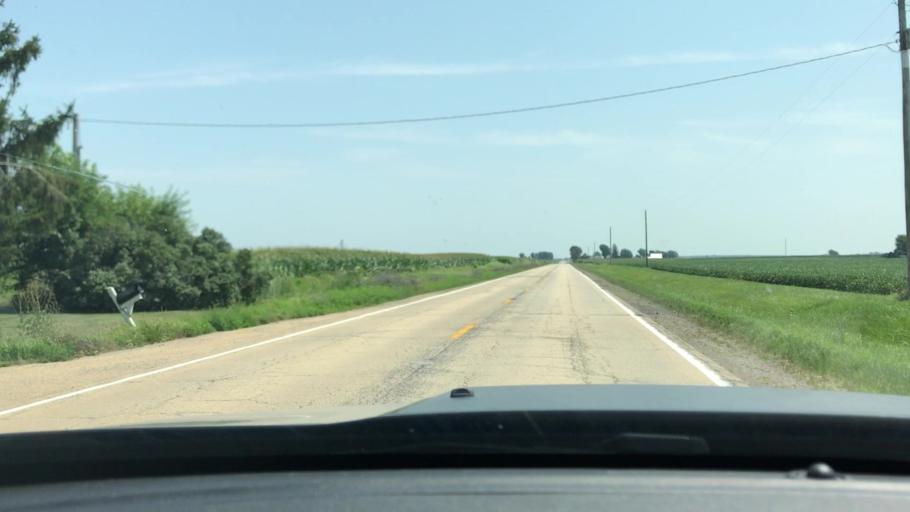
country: US
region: Illinois
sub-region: LaSalle County
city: Ottawa
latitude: 41.4702
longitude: -88.8571
